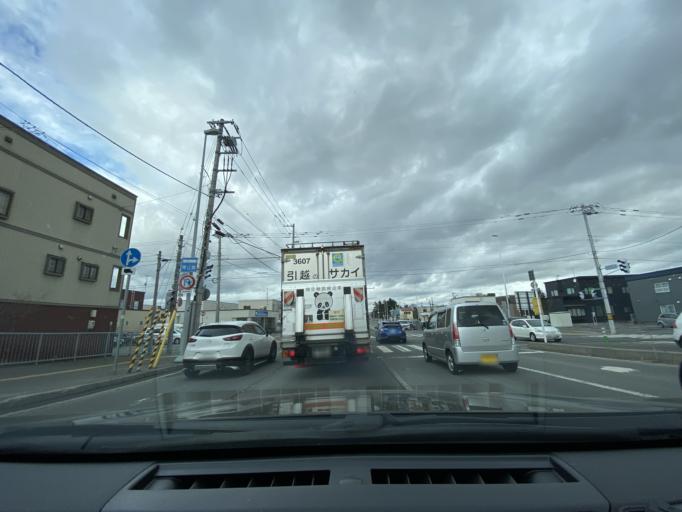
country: JP
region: Hokkaido
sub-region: Asahikawa-shi
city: Asahikawa
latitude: 43.7841
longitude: 142.3665
